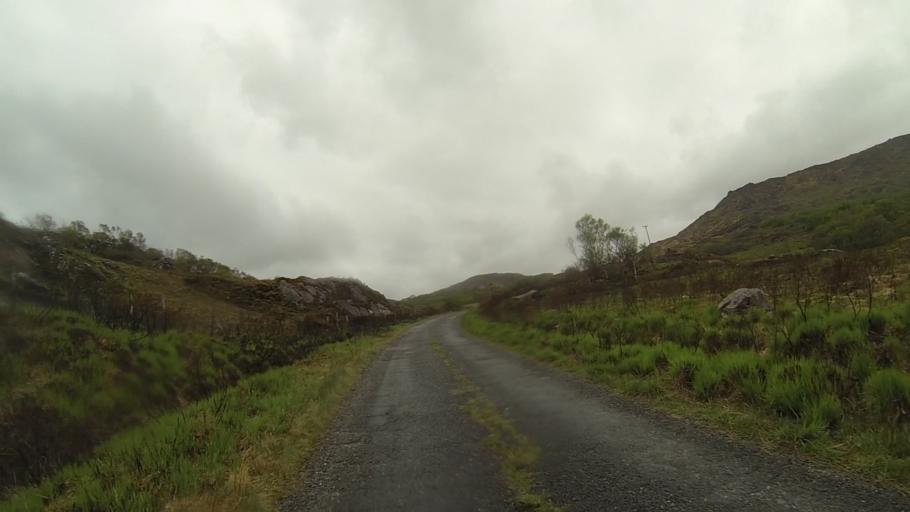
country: IE
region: Munster
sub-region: Ciarrai
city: Kenmare
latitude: 51.9697
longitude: -9.6363
